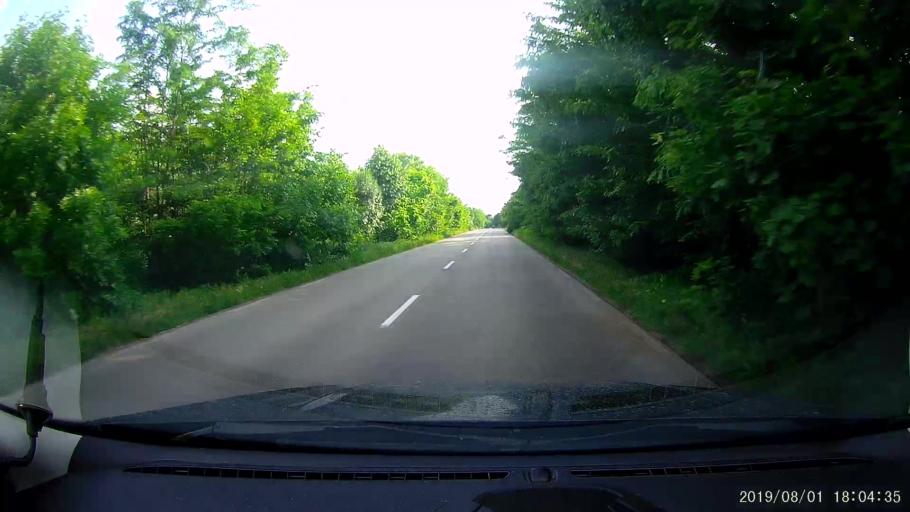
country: BG
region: Silistra
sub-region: Obshtina Alfatar
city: Alfatar
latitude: 43.9062
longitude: 27.2766
